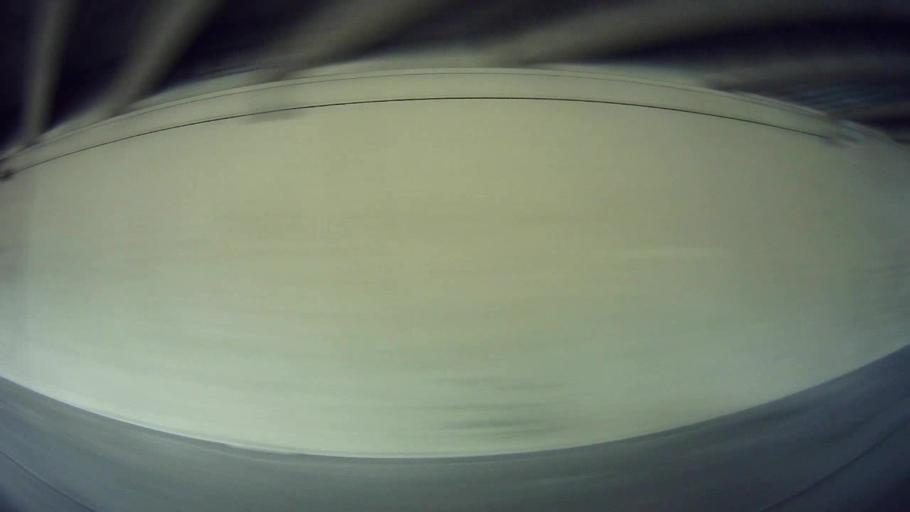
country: US
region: Michigan
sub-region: Oakland County
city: Oak Park
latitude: 42.4141
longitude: -83.1700
